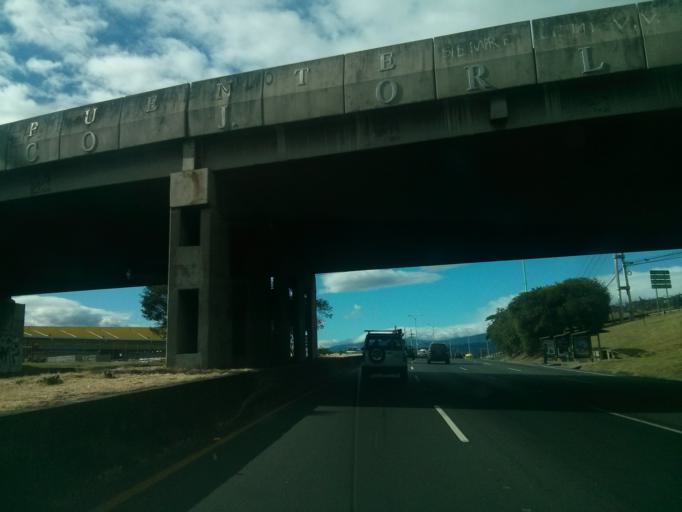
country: CR
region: Heredia
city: La Asuncion
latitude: 9.9810
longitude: -84.1617
